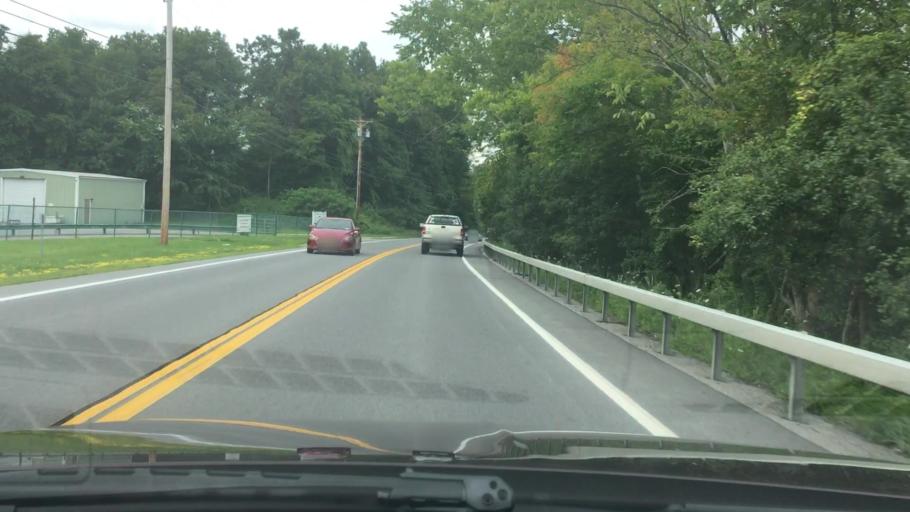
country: US
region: New York
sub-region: Dutchess County
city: Hillside Lake
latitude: 41.6483
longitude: -73.7271
